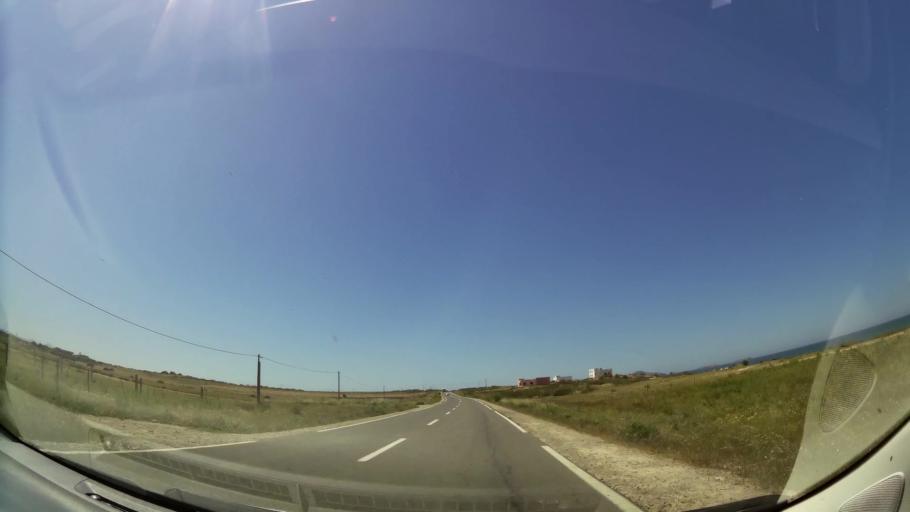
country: MA
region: Oriental
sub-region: Berkane-Taourirt
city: Madagh
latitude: 35.1254
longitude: -2.3874
